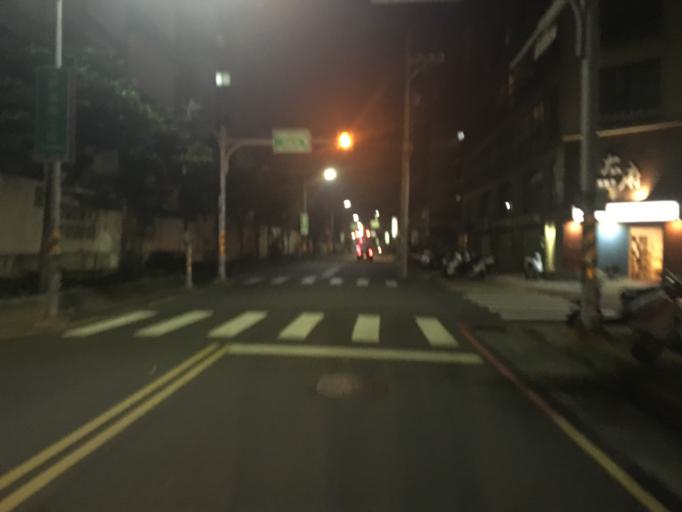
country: TW
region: Taiwan
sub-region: Hsinchu
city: Hsinchu
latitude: 24.8209
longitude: 120.9733
